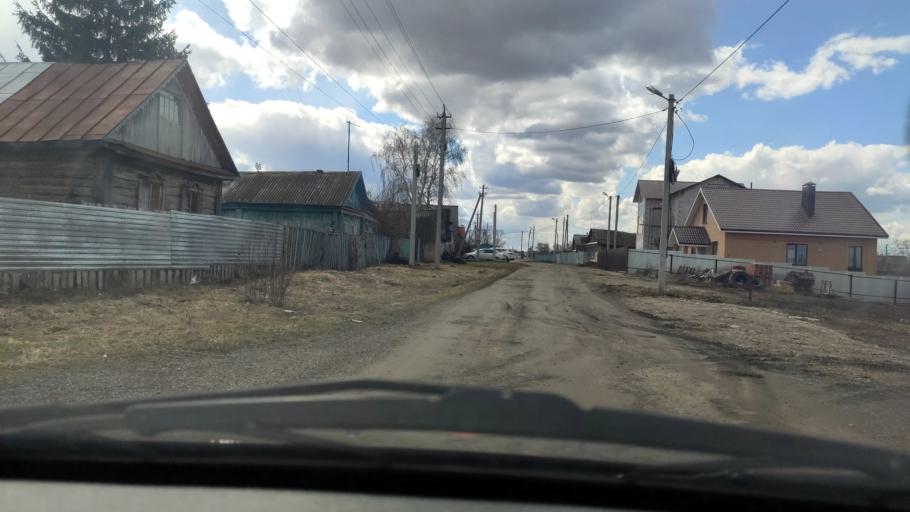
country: RU
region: Bashkortostan
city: Kabakovo
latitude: 54.6231
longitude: 56.1154
